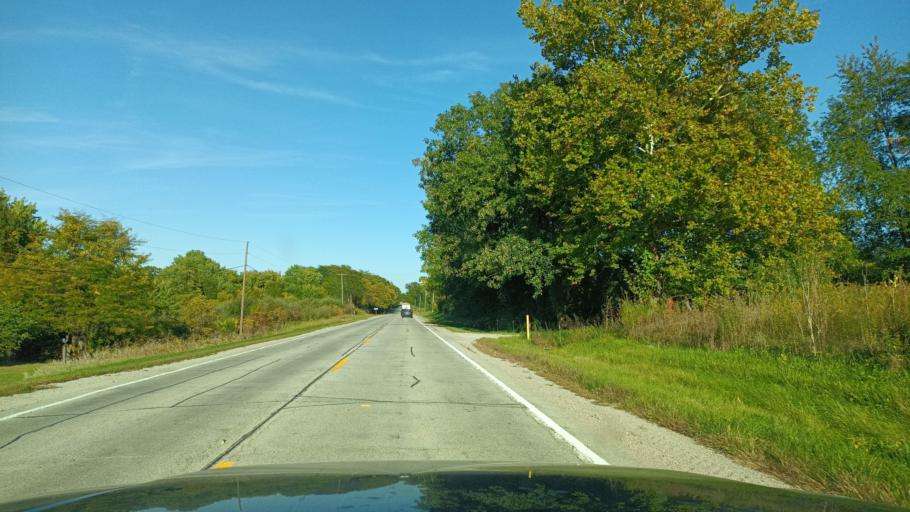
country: US
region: Illinois
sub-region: De Witt County
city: Farmer City
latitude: 40.2262
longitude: -88.6897
